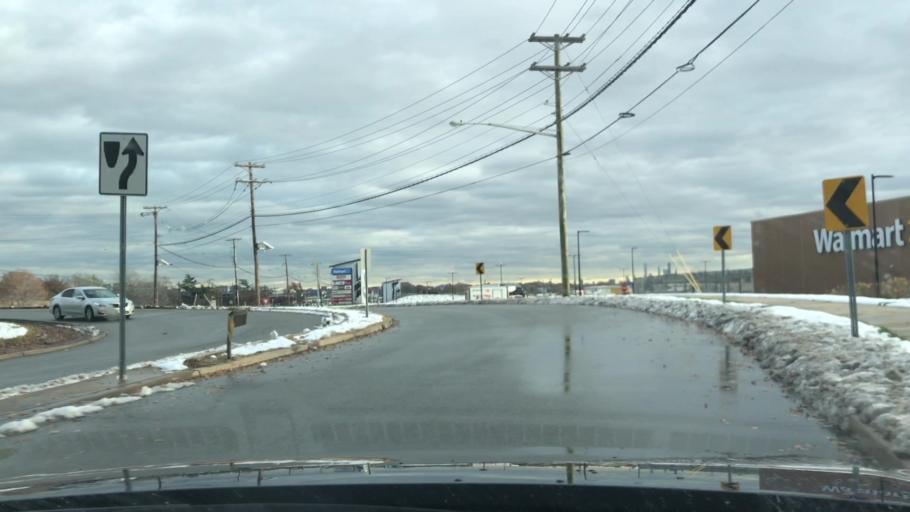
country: US
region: New Jersey
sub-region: Bergen County
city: Hasbrouck Heights
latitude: 40.8636
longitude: -74.0621
